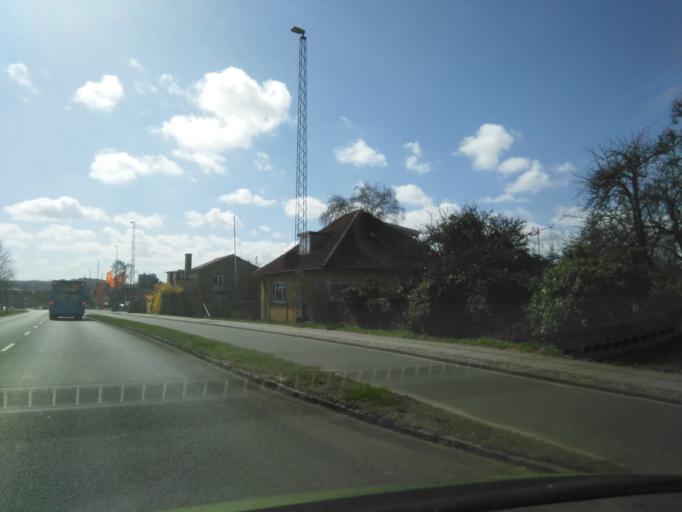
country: DK
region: Central Jutland
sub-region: Arhus Kommune
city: Arhus
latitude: 56.1335
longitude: 10.1699
